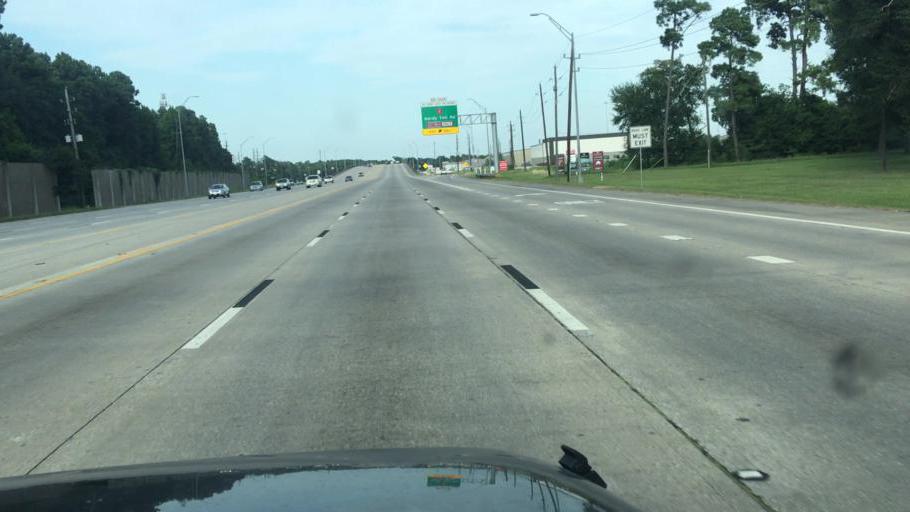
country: US
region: Texas
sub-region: Harris County
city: Spring
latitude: 30.0251
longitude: -95.4123
